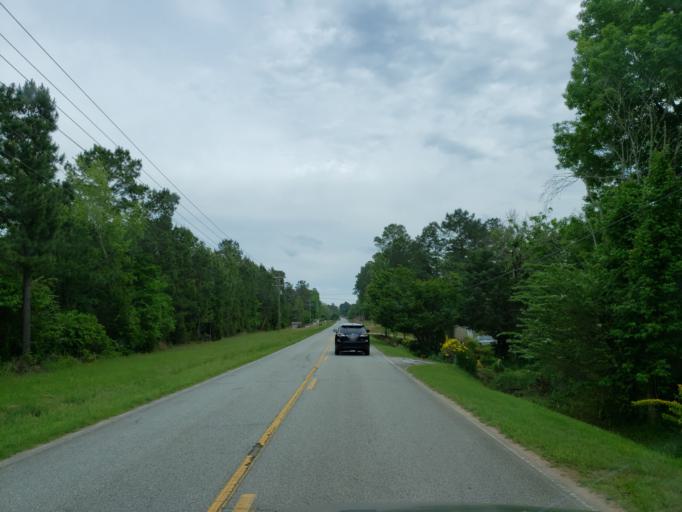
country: US
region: Georgia
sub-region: Bibb County
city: West Point
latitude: 32.8145
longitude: -83.8512
